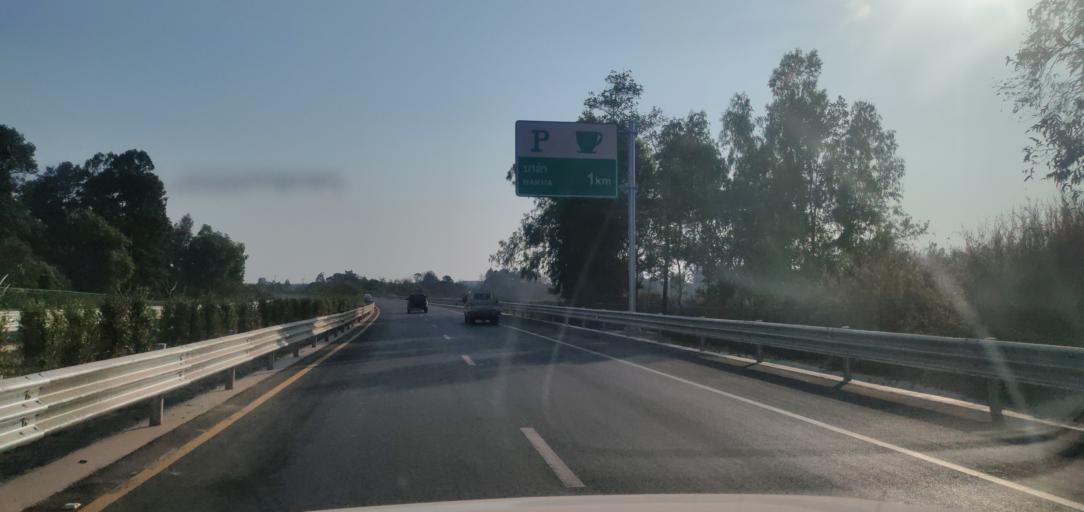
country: TH
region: Nong Khai
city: Sangkhom
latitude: 18.2258
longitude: 102.4811
